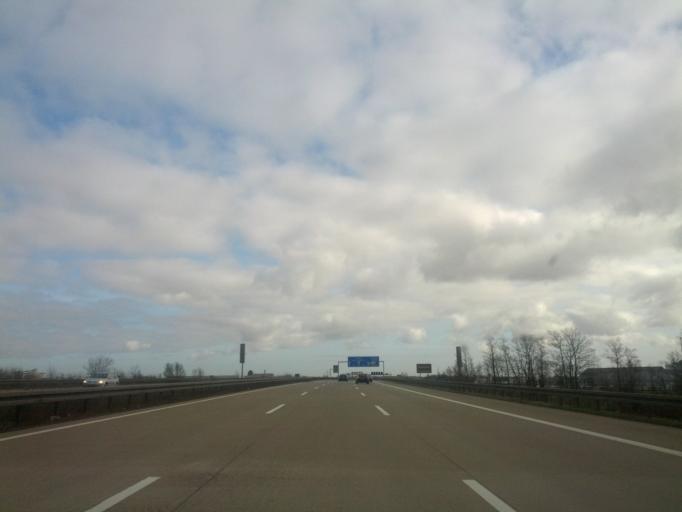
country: DE
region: Lower Saxony
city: Laatzen
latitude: 52.3475
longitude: 9.8721
